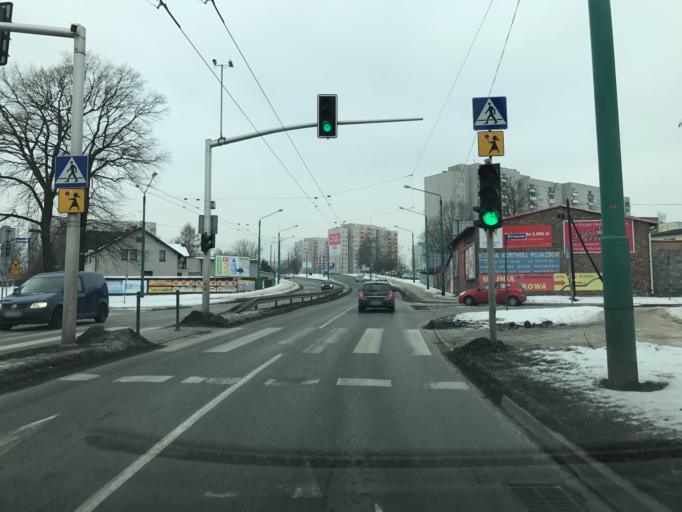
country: PL
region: Silesian Voivodeship
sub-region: Tychy
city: Cielmice
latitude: 50.1017
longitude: 18.9977
